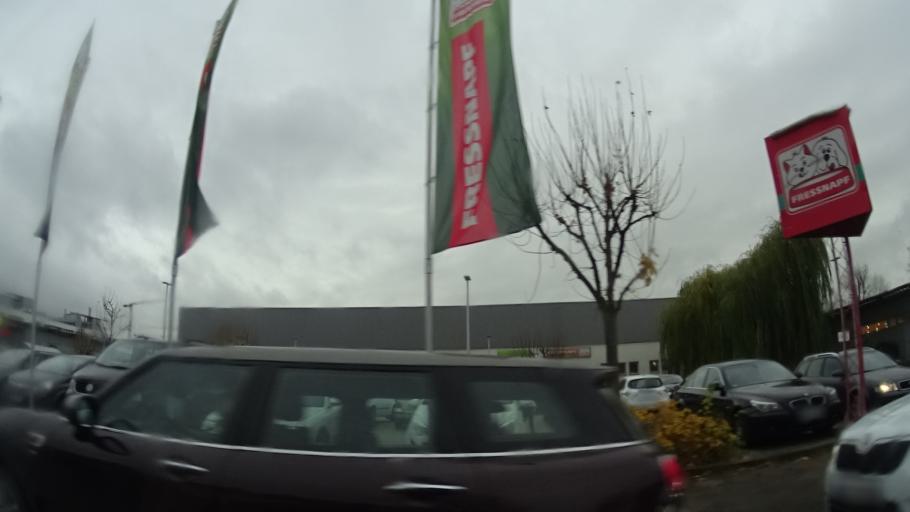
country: DE
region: Baden-Wuerttemberg
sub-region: Karlsruhe Region
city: Karlsruhe
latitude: 49.0083
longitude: 8.4395
